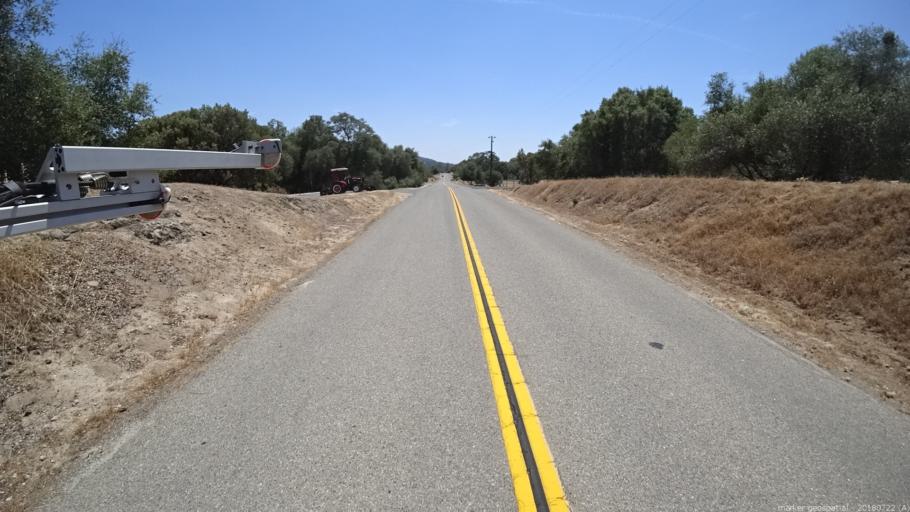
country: US
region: California
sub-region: Madera County
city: Yosemite Lakes
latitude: 37.2127
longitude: -119.7289
